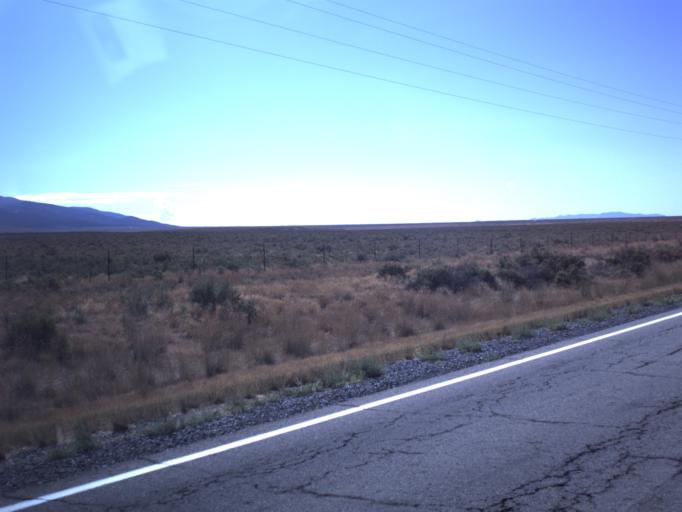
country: US
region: Utah
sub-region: Tooele County
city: Tooele
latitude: 40.4023
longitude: -112.3859
